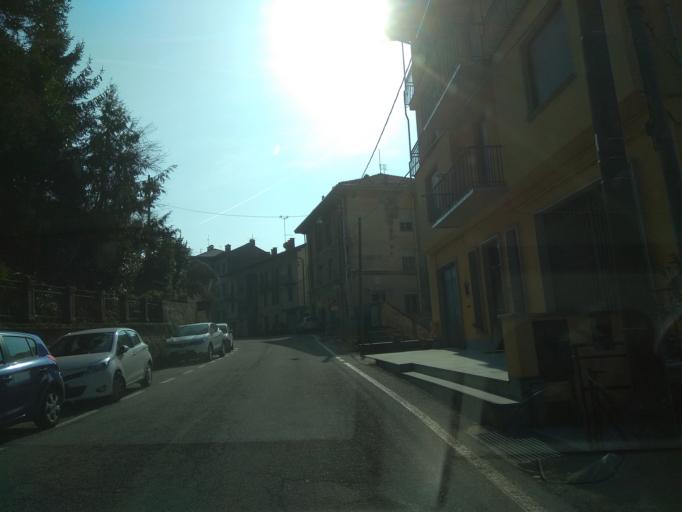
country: IT
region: Piedmont
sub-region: Provincia di Biella
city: Mosso Santa Maria
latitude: 45.6476
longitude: 8.1346
